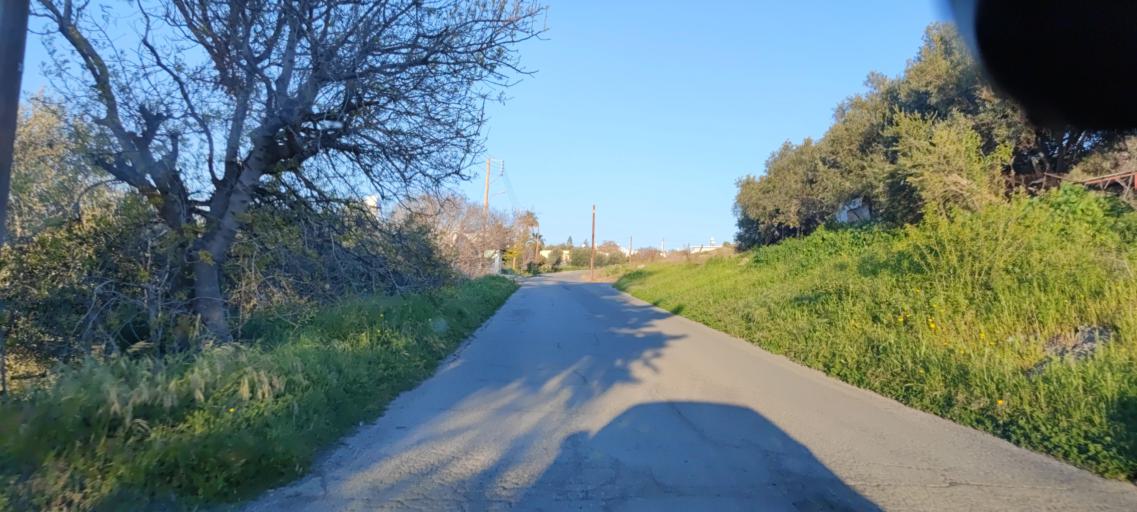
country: CY
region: Pafos
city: Chlorakas
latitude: 34.7838
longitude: 32.4107
